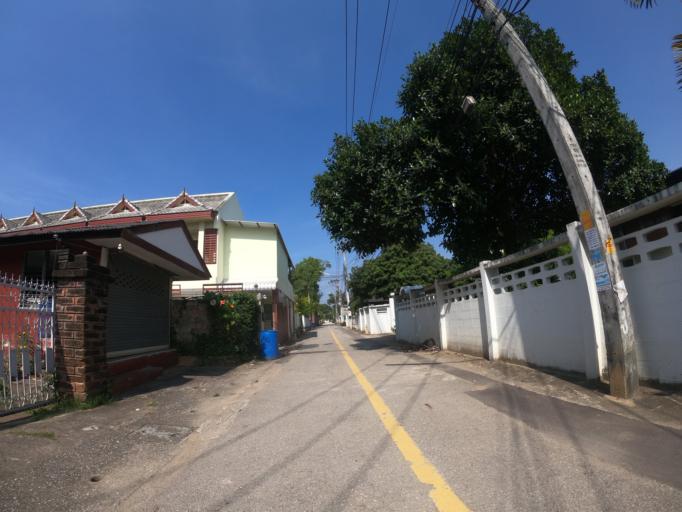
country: TH
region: Chiang Mai
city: Chiang Mai
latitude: 18.7710
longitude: 99.0036
